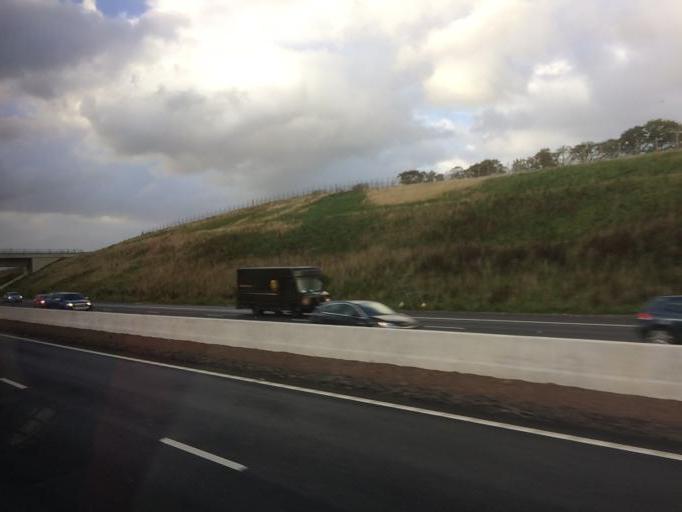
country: GB
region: Scotland
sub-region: North Lanarkshire
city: Coatbridge
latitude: 55.8397
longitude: -4.0379
